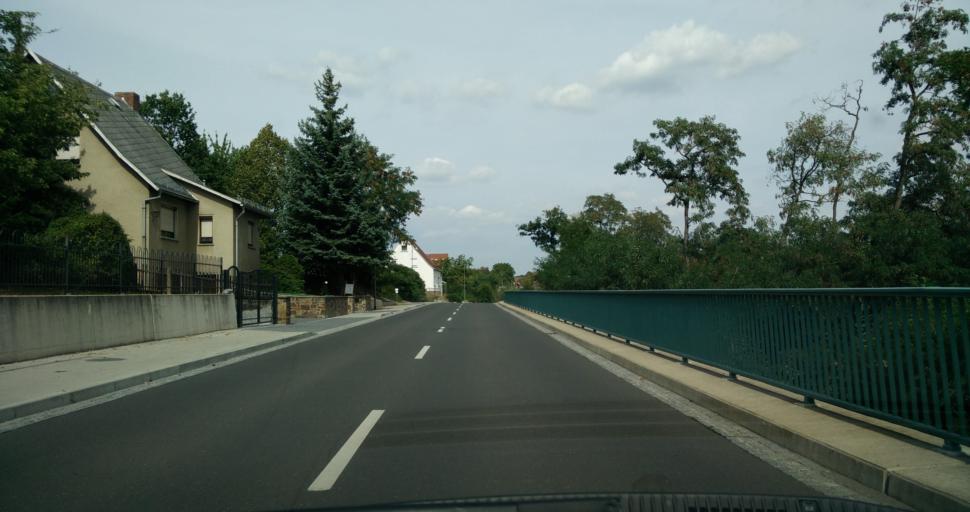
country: DE
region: Saxony
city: Colditz
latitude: 51.1272
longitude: 12.7980
